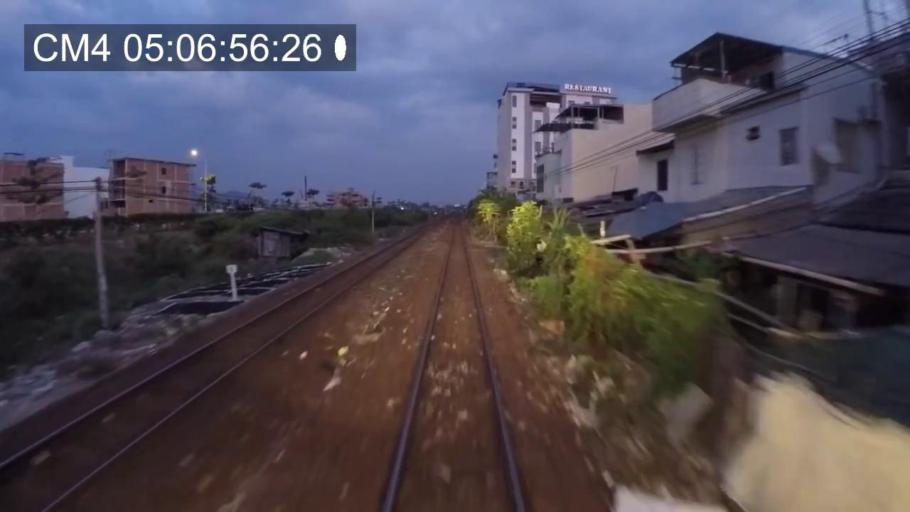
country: VN
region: Khanh Hoa
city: Nha Trang
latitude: 12.2815
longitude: 109.1822
